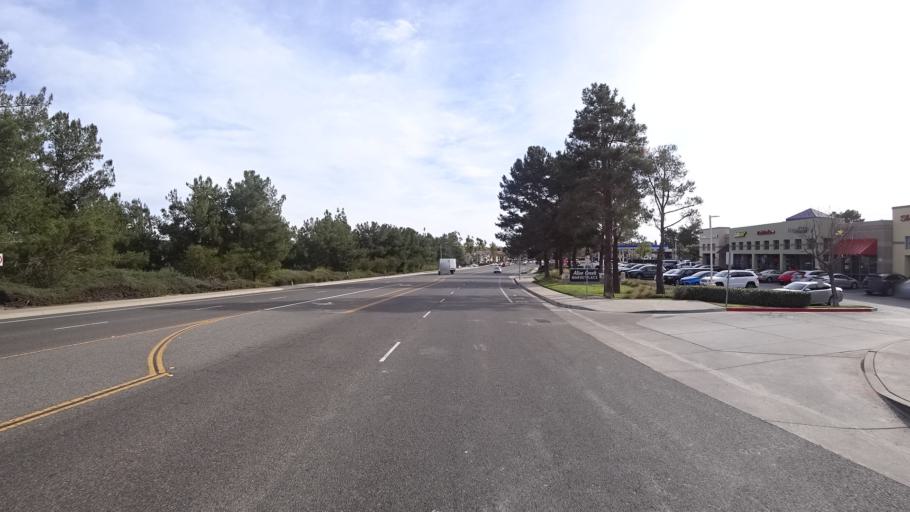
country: US
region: California
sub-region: Orange County
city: Laguna Woods
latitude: 33.5887
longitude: -117.7215
